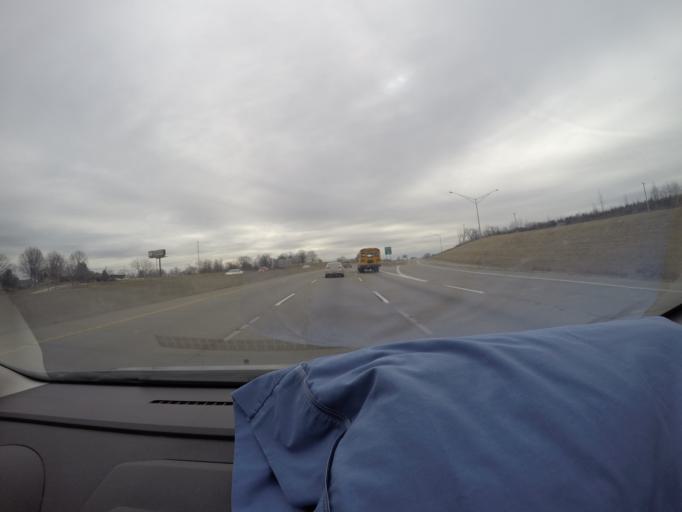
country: US
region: Missouri
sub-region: Saint Louis County
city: Normandy
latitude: 38.7204
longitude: -90.3043
